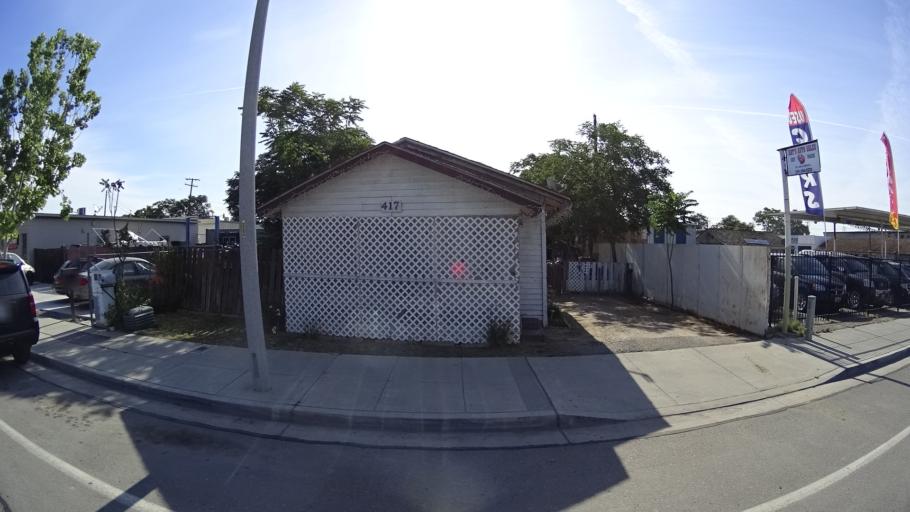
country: US
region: California
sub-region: Kings County
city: Hanford
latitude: 36.3295
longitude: -119.6370
